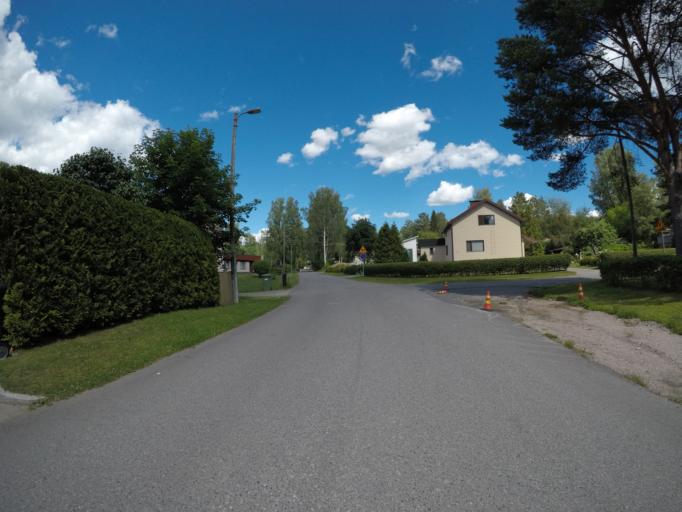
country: FI
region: Haeme
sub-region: Haemeenlinna
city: Haemeenlinna
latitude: 61.0085
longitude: 24.4366
